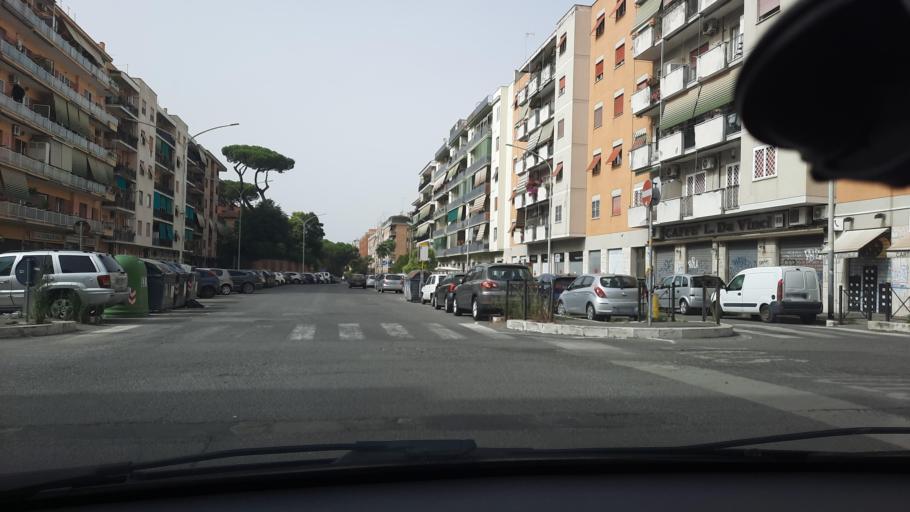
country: IT
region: Latium
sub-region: Citta metropolitana di Roma Capitale
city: Rome
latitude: 41.8526
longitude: 12.4801
